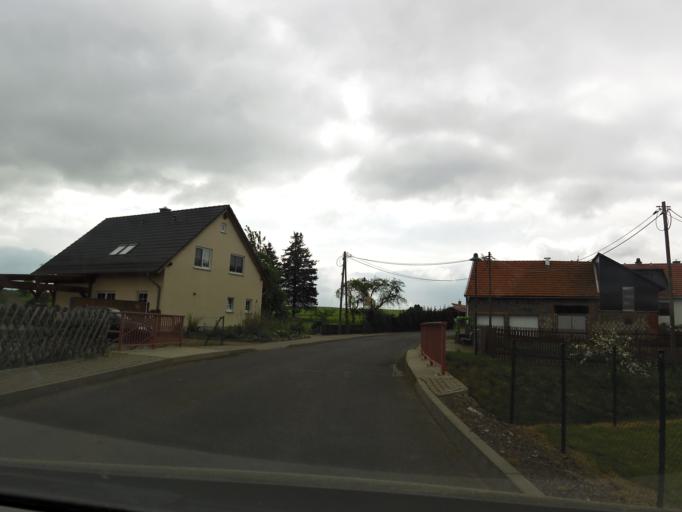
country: DE
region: Thuringia
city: Ernstroda
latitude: 50.8797
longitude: 10.6147
